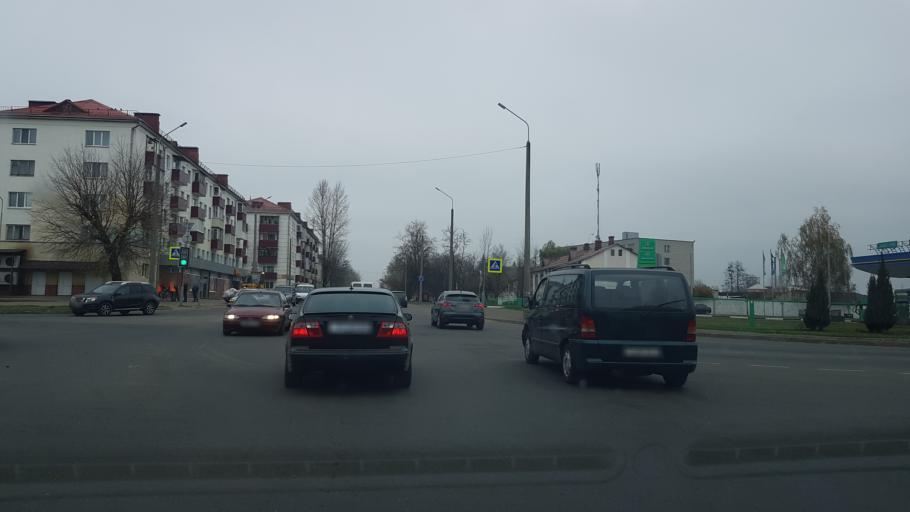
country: BY
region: Mogilev
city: Babruysk
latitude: 53.1591
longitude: 29.2335
